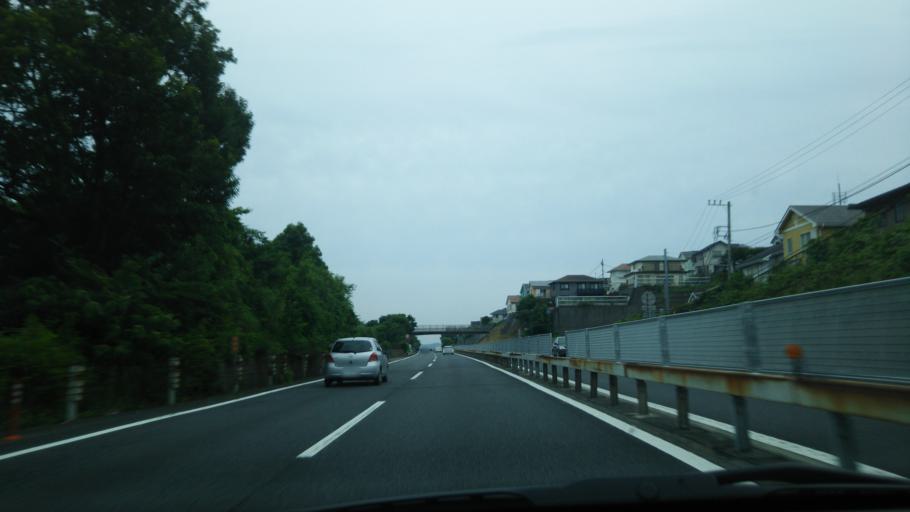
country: JP
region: Kanagawa
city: Oiso
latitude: 35.3395
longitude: 139.2961
